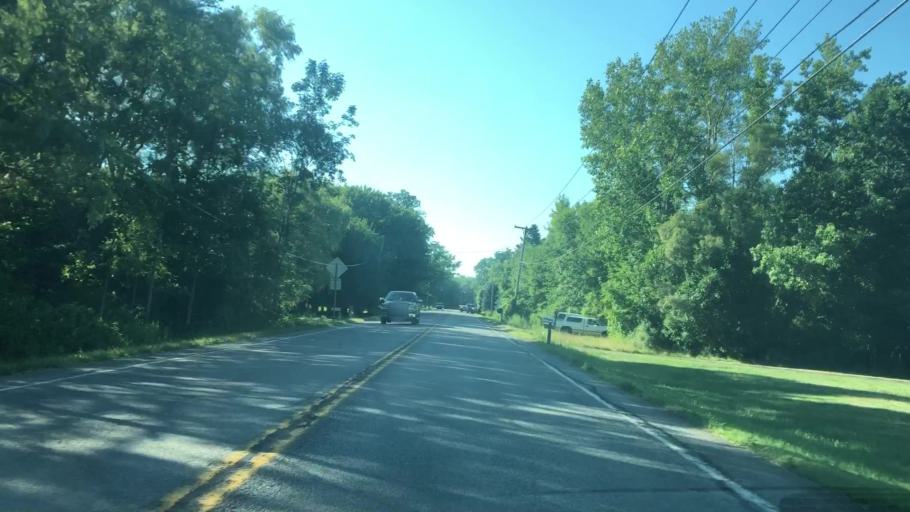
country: US
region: New York
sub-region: Wayne County
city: Ontario
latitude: 43.1811
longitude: -77.2865
